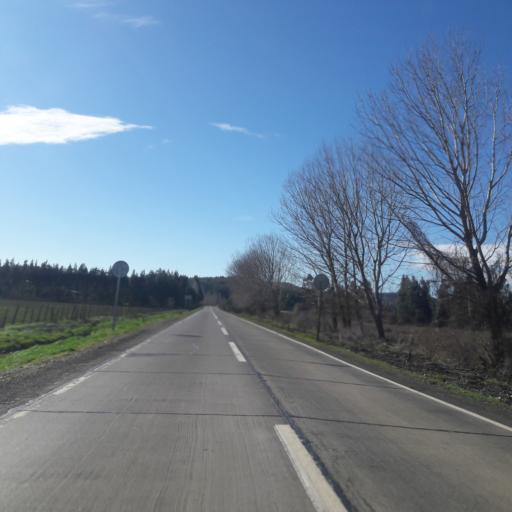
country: CL
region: Araucania
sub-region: Provincia de Malleco
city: Collipulli
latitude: -37.7844
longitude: -72.5238
